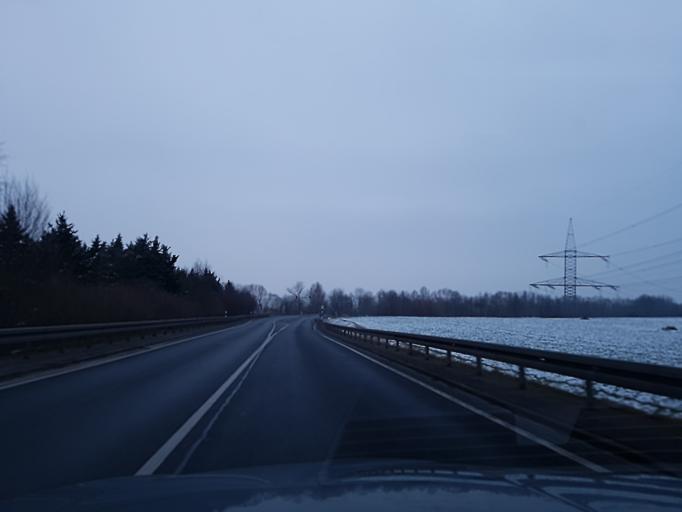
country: DE
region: Saxony
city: Ostrau
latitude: 51.2015
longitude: 13.1541
